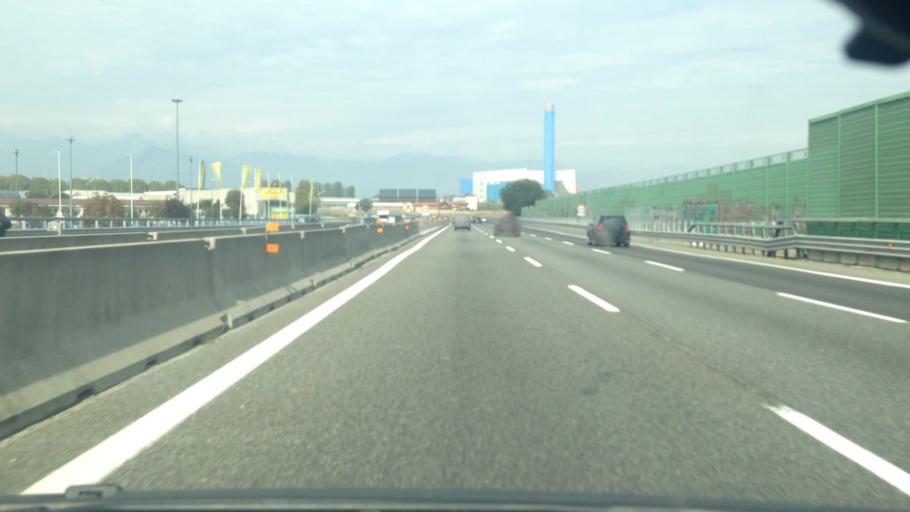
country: IT
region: Piedmont
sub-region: Provincia di Torino
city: Fornaci
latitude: 45.0279
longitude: 7.5931
